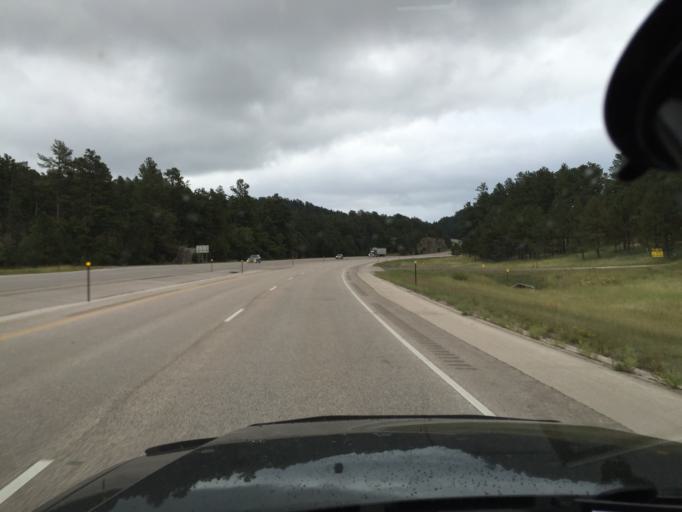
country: US
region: South Dakota
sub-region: Pennington County
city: Colonial Pine Hills
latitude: 43.9434
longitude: -103.3942
